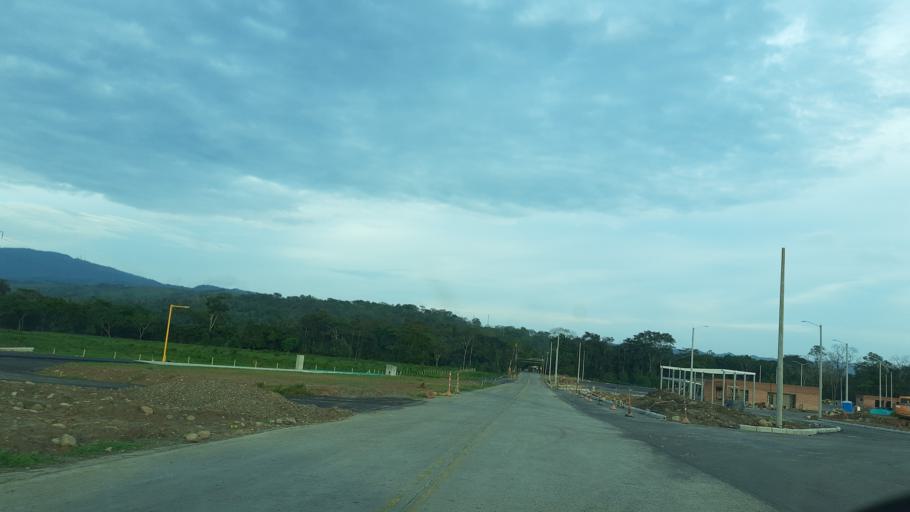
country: CO
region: Casanare
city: Sabanalarga
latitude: 4.8247
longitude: -73.0802
